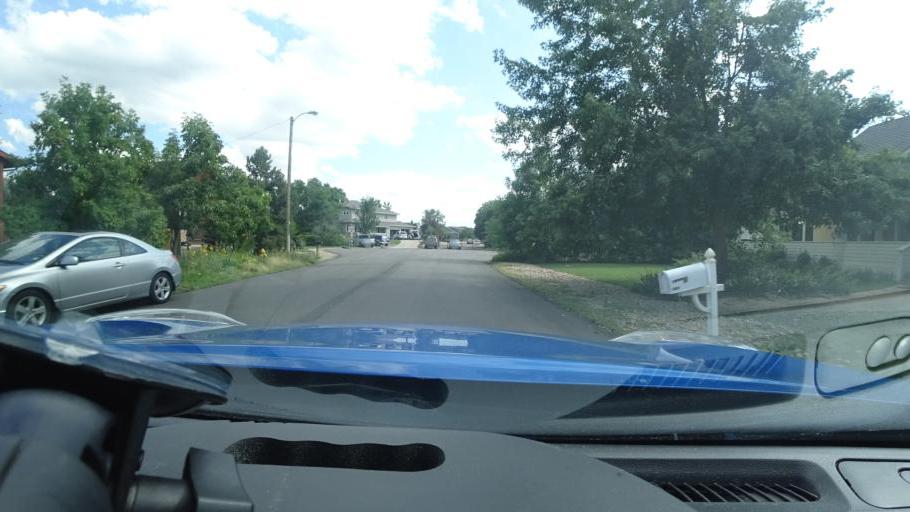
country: US
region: Colorado
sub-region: Adams County
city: Aurora
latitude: 39.6981
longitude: -104.8718
